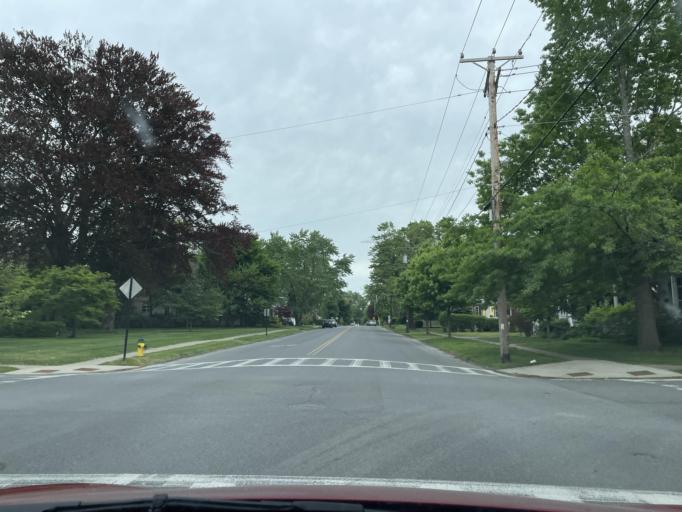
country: US
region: New York
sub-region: Ulster County
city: Saugerties
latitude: 42.0819
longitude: -73.9518
